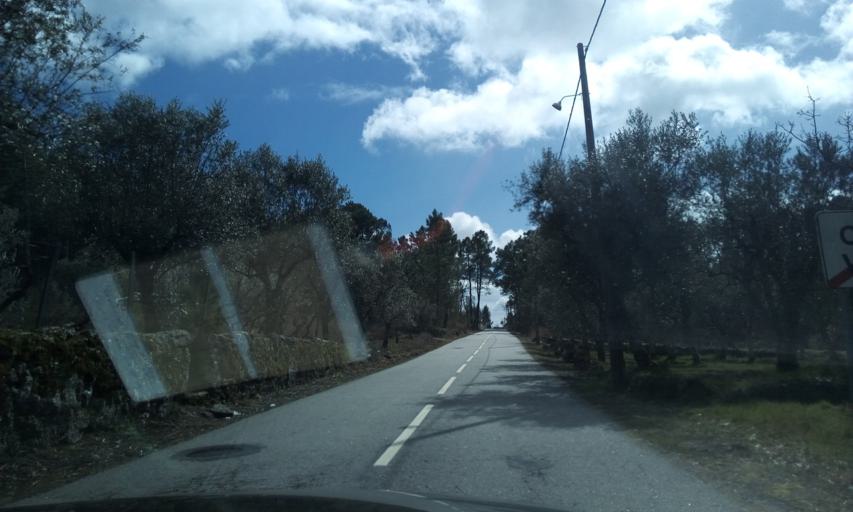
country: PT
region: Guarda
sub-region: Fornos de Algodres
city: Fornos de Algodres
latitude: 40.6441
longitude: -7.5479
